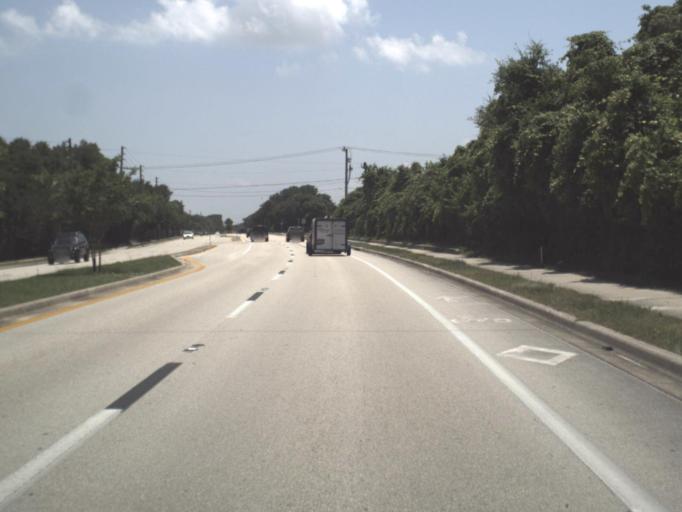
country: US
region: Florida
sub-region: Saint Johns County
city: Saint Augustine Beach
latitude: 29.8422
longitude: -81.2767
